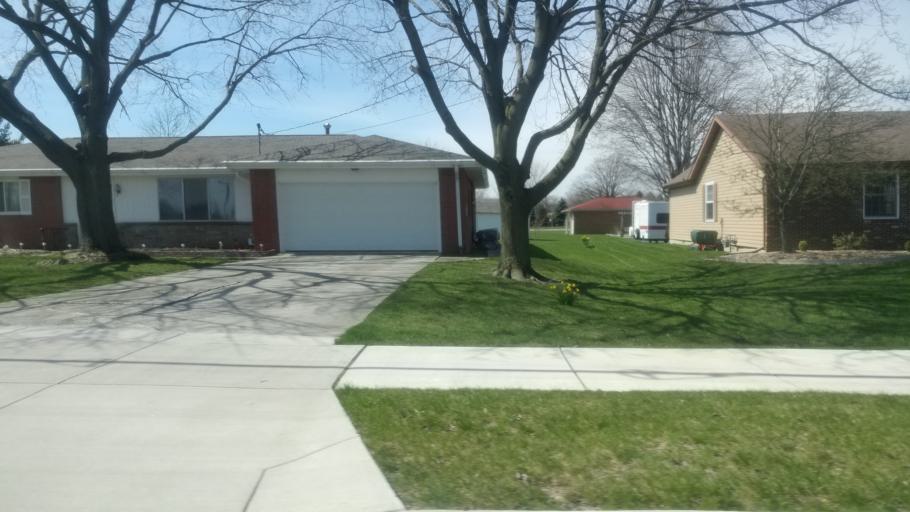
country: US
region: Ohio
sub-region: Wood County
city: Bowling Green
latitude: 41.3853
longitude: -83.6678
